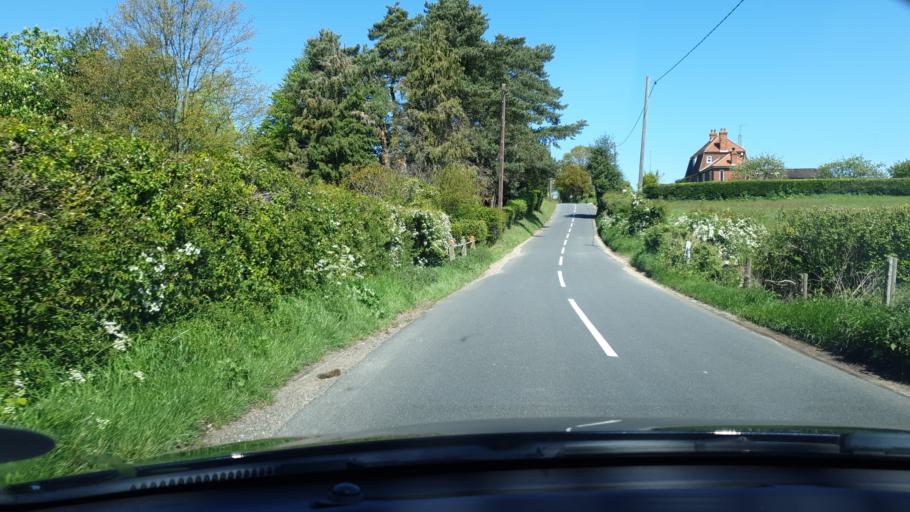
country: GB
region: England
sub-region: Essex
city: Little Clacton
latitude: 51.8628
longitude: 1.1200
